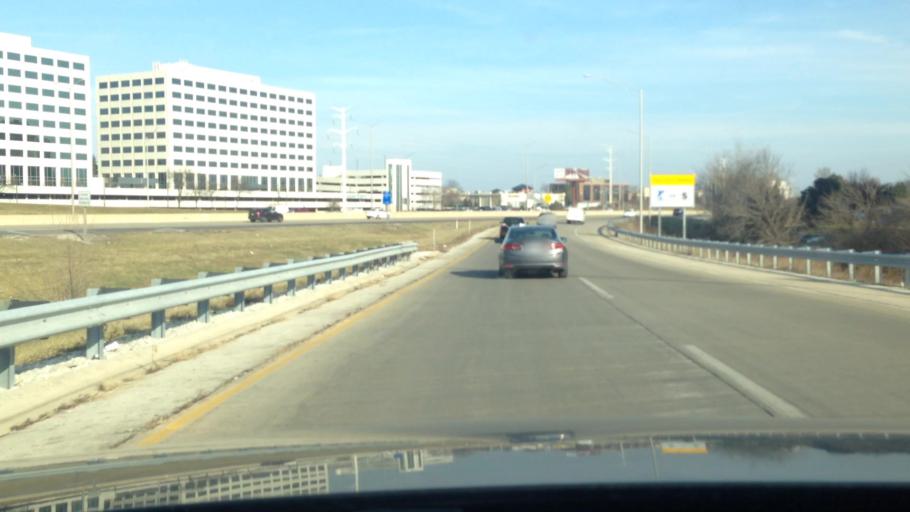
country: US
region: Illinois
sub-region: DuPage County
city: Downers Grove
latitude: 41.8332
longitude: -88.0092
